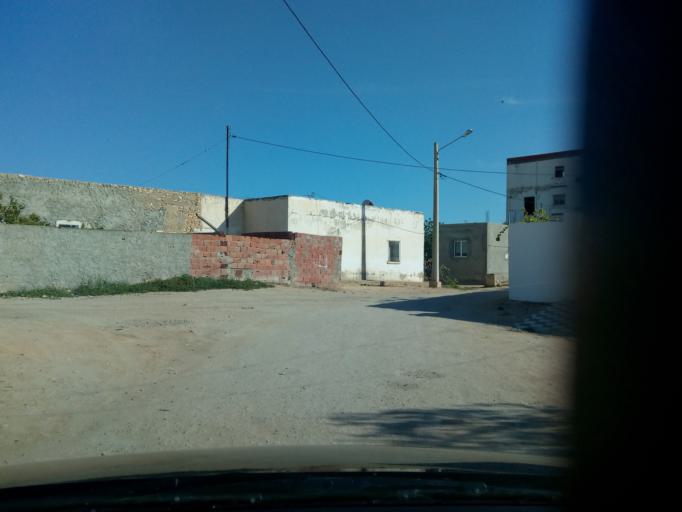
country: TN
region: Safaqis
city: Sfax
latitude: 34.7299
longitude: 10.6113
